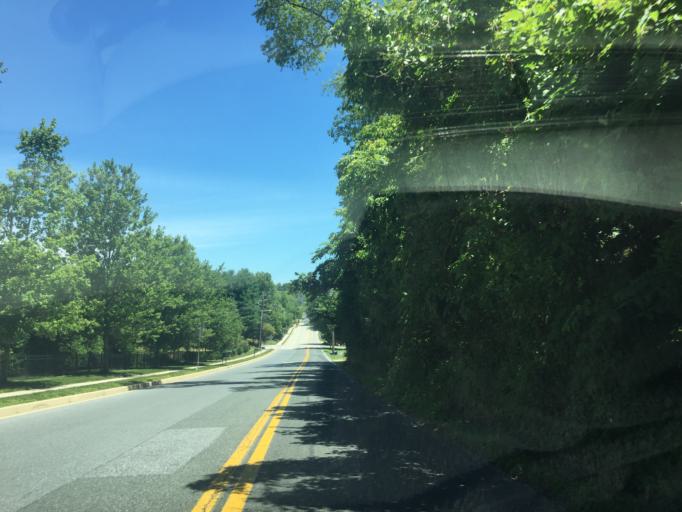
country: US
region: Maryland
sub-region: Baltimore County
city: Garrison
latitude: 39.3893
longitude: -76.7467
